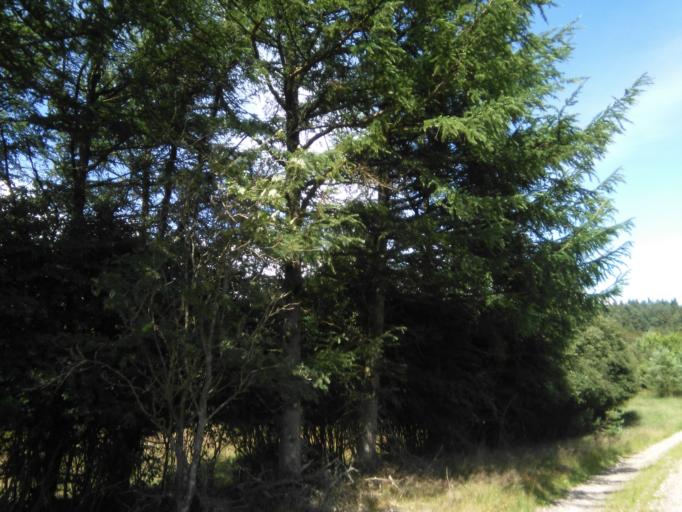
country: DK
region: Central Jutland
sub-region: Silkeborg Kommune
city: Virklund
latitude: 56.0741
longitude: 9.4515
